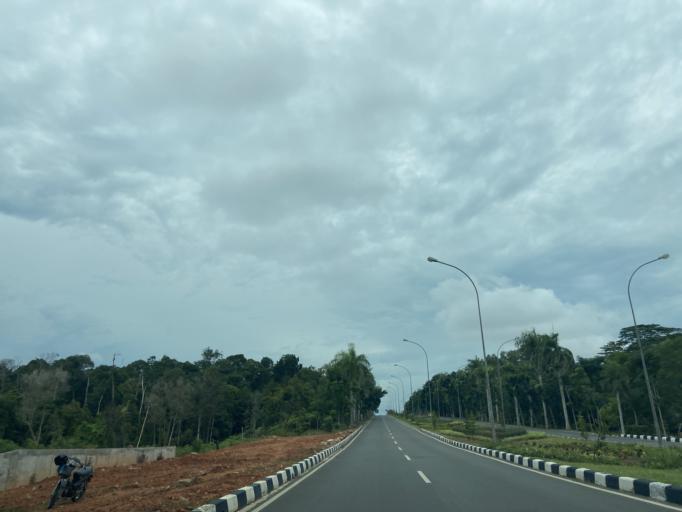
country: SG
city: Singapore
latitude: 1.1266
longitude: 104.1088
